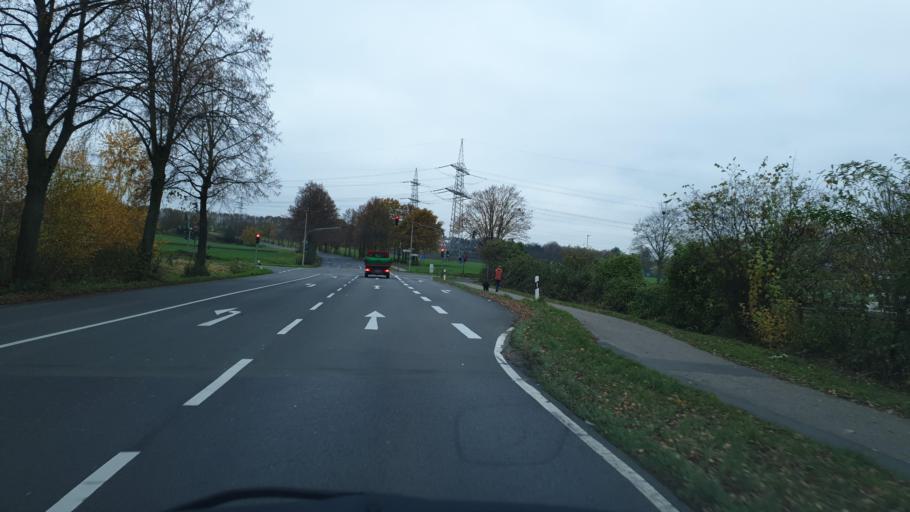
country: DE
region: North Rhine-Westphalia
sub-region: Regierungsbezirk Koln
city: Hurth
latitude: 50.8855
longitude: 6.8529
